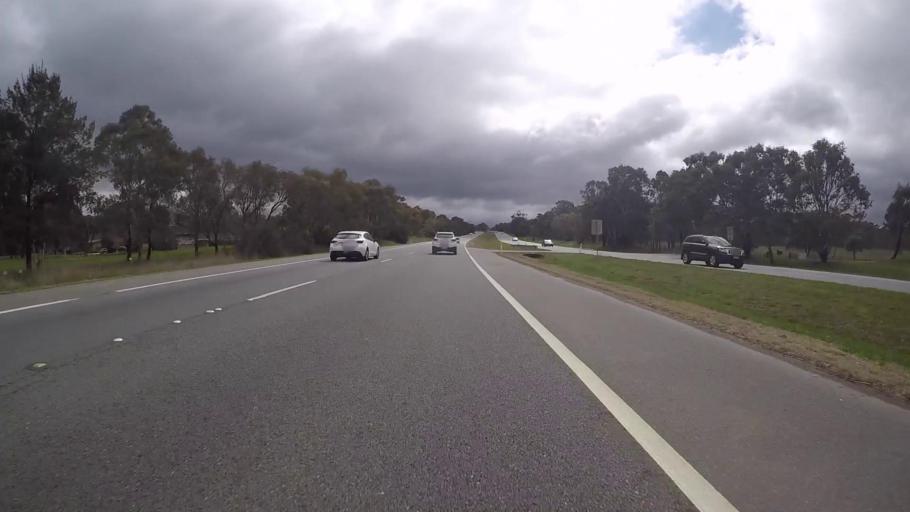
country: AU
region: Australian Capital Territory
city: Kaleen
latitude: -35.2152
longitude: 149.1142
